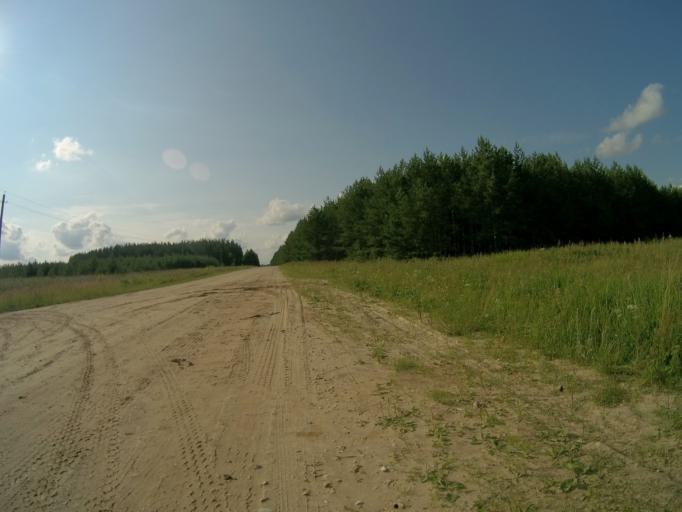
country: RU
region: Vladimir
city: Orgtrud
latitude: 56.3268
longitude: 40.7130
